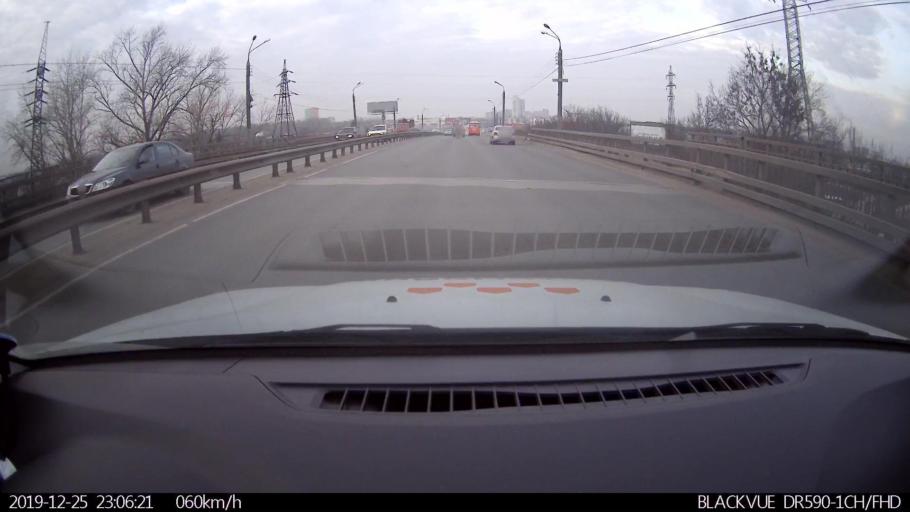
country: RU
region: Nizjnij Novgorod
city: Nizhniy Novgorod
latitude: 56.3067
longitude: 43.9049
